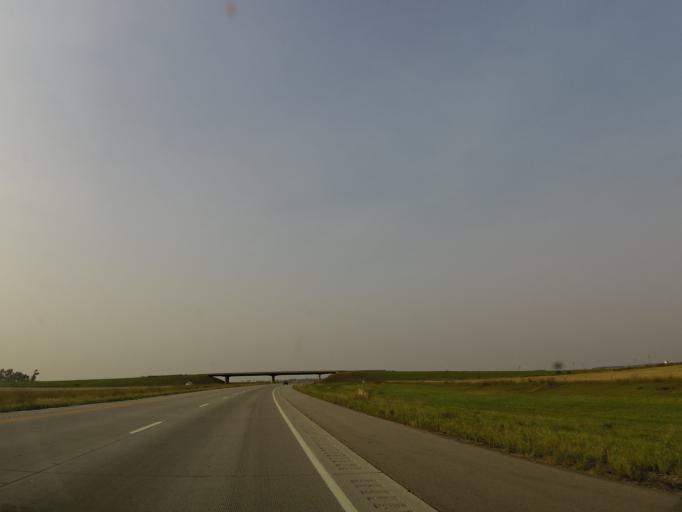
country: US
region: North Dakota
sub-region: Cass County
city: West Fargo
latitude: 47.1054
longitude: -96.9578
